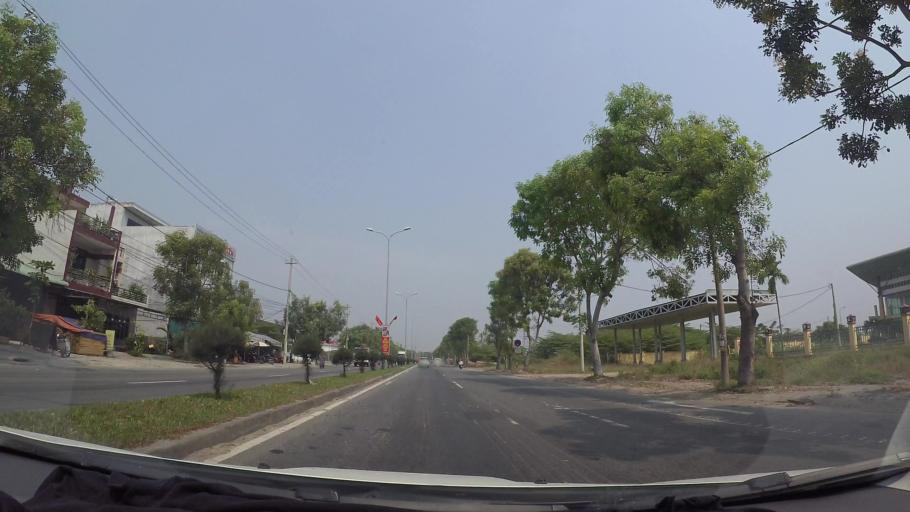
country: VN
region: Da Nang
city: Cam Le
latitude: 15.9676
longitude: 108.2106
